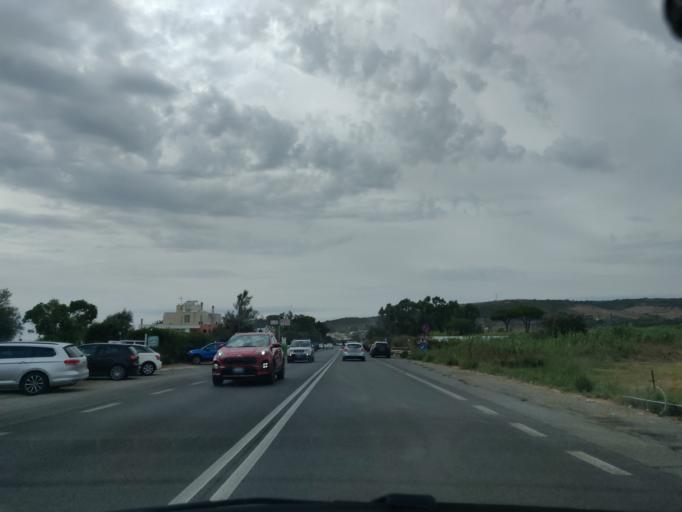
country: IT
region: Latium
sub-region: Citta metropolitana di Roma Capitale
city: Santa Marinella
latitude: 42.0375
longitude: 11.9209
